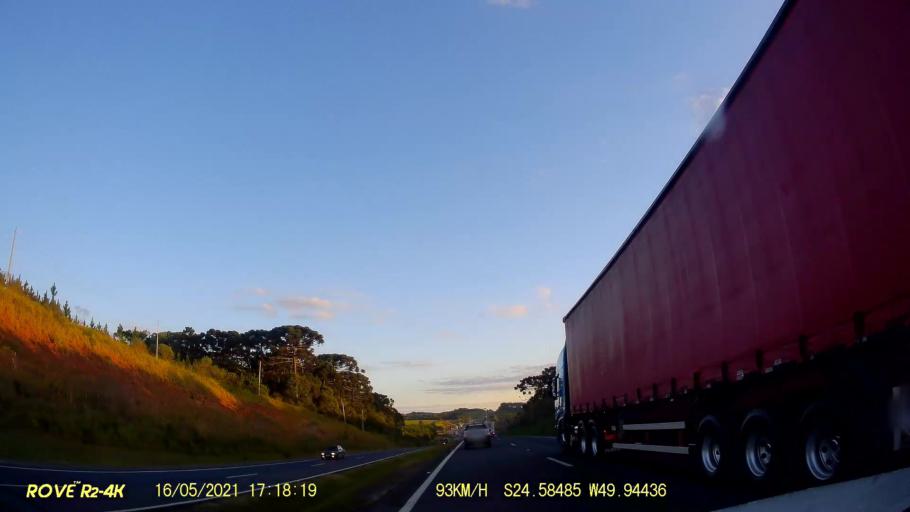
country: BR
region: Parana
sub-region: Pirai Do Sul
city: Pirai do Sul
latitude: -24.5852
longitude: -49.9445
